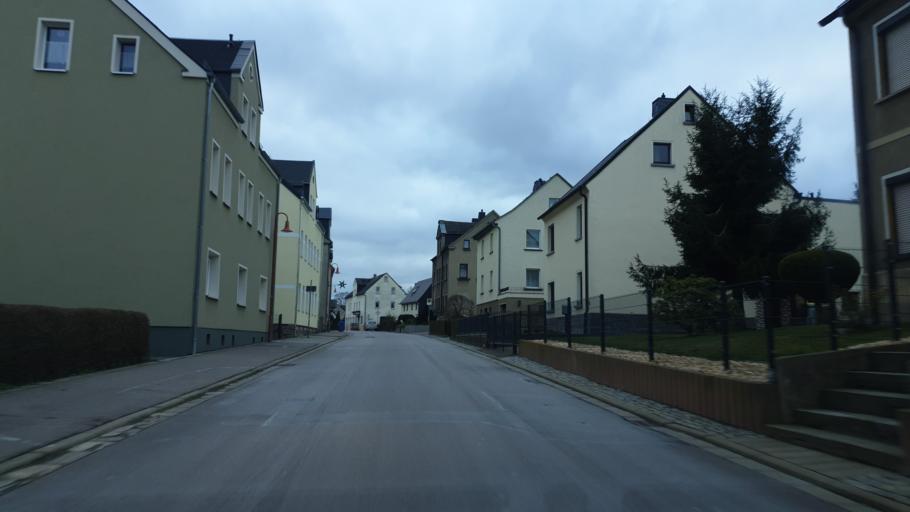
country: DE
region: Saxony
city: Hohndorf
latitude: 50.7385
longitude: 12.6610
